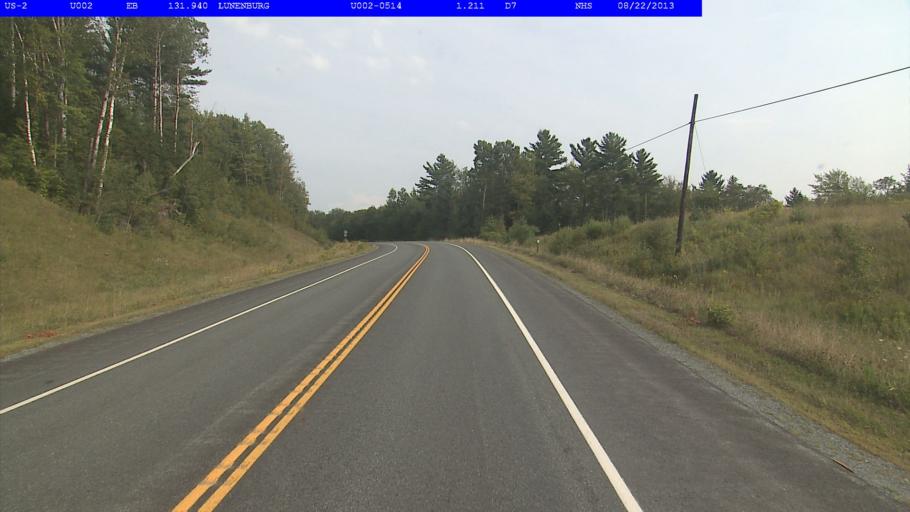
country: US
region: New Hampshire
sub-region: Grafton County
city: Littleton
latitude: 44.4674
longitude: -71.7507
